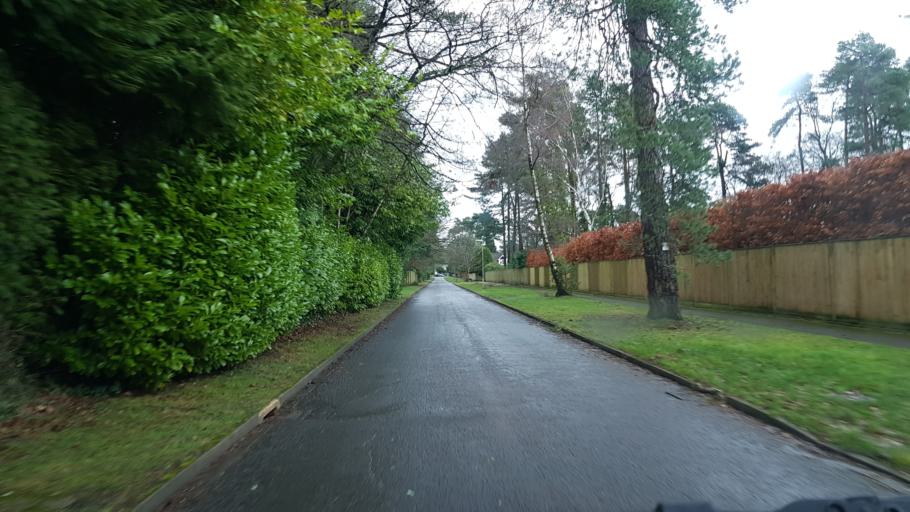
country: GB
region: England
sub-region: Surrey
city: Hindhead
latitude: 51.1060
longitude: -0.7538
